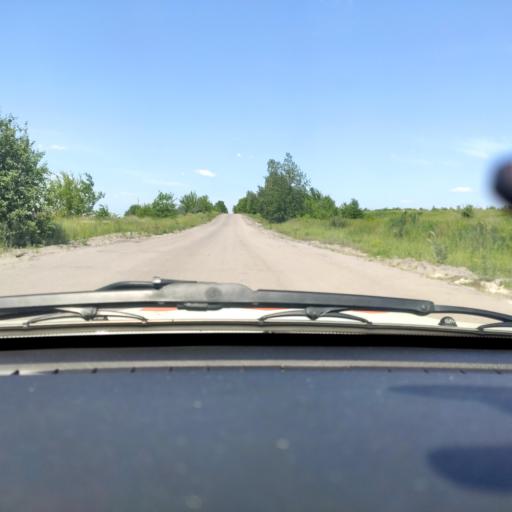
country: RU
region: Voronezj
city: Devitsa
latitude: 51.6263
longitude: 38.9524
